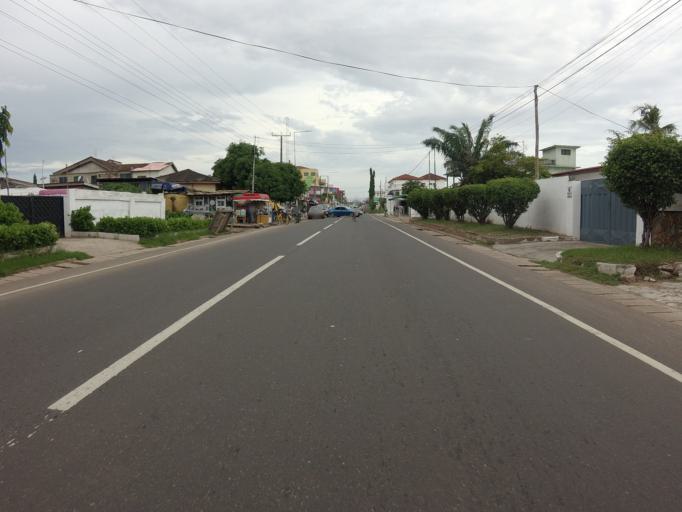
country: GH
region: Greater Accra
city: Dome
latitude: 5.6096
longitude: -0.2055
